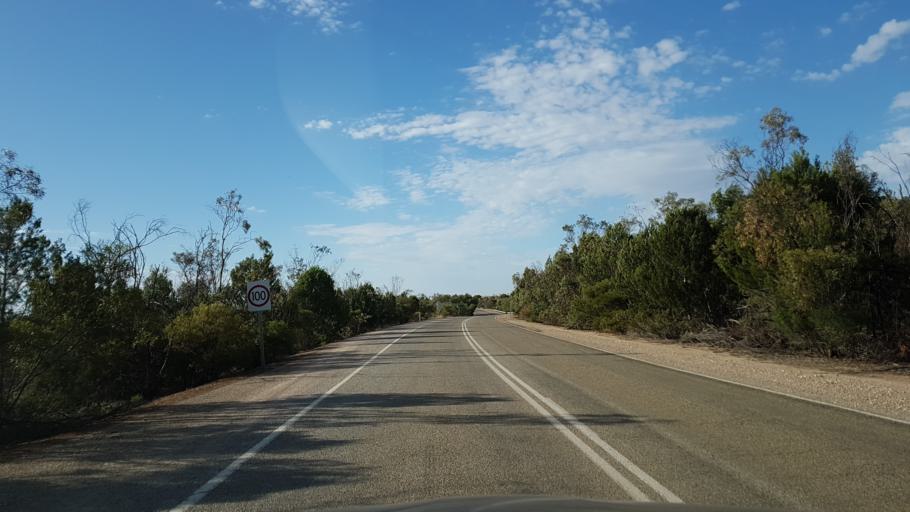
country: AU
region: South Australia
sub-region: Clare and Gilbert Valleys
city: Clare
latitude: -33.7045
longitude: 138.4051
